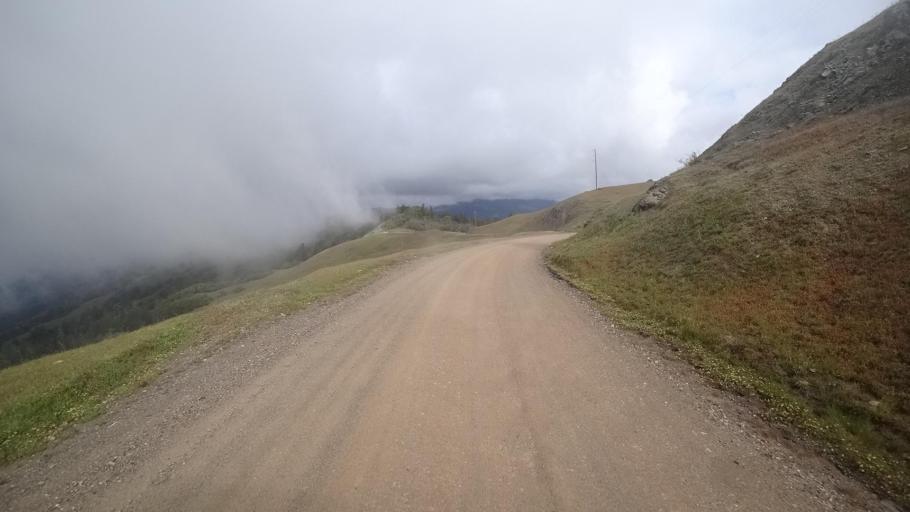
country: US
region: California
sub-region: Humboldt County
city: Redway
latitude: 40.2001
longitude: -123.7109
